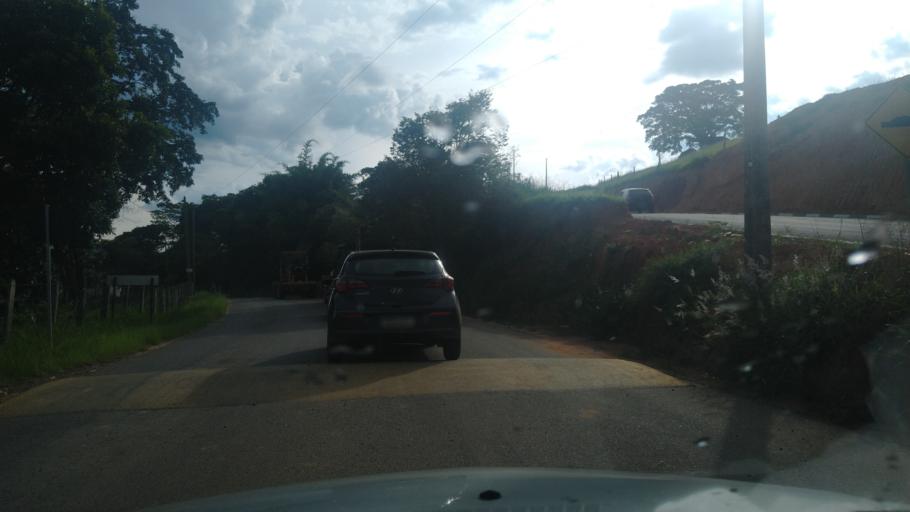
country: BR
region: Minas Gerais
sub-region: Extrema
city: Extrema
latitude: -22.7385
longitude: -46.3705
